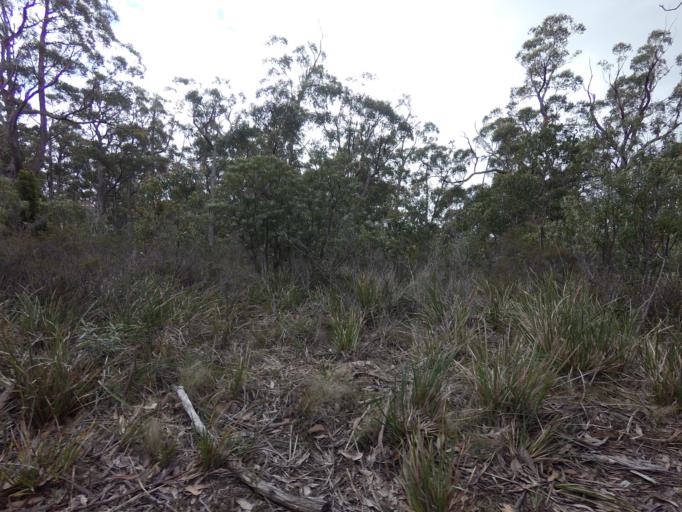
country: AU
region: Tasmania
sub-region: Huon Valley
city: Geeveston
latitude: -43.4639
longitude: 146.9182
